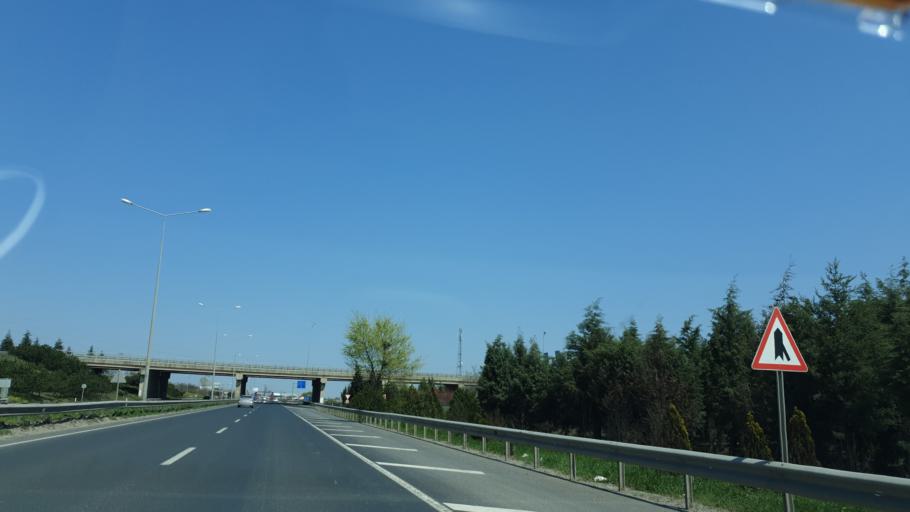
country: TR
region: Tekirdag
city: Corlu
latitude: 41.1768
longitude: 27.8074
